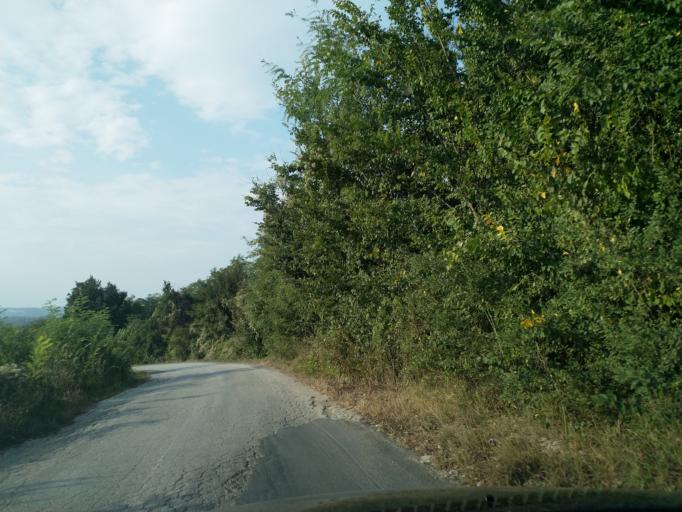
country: RS
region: Central Serbia
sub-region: Pomoravski Okrug
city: Paracin
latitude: 43.8434
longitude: 21.5294
